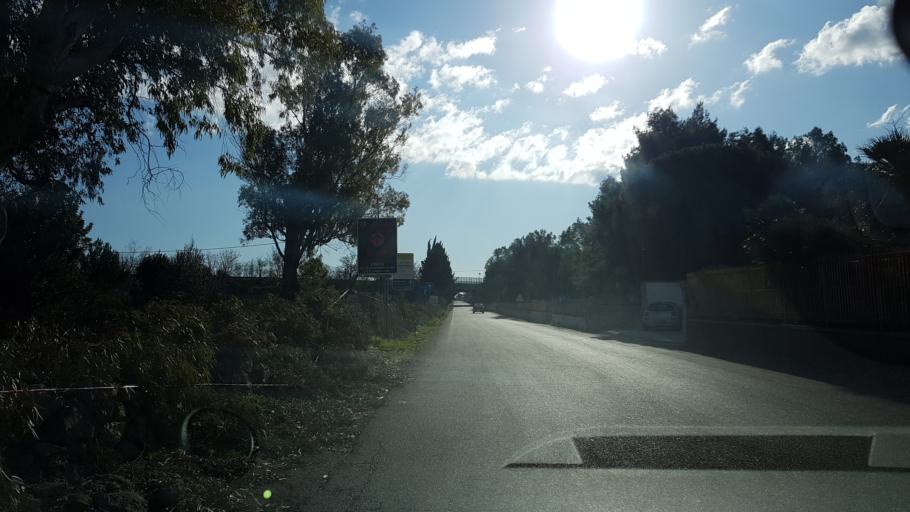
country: IT
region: Apulia
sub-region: Provincia di Lecce
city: Castromediano
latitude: 40.3281
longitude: 18.1834
